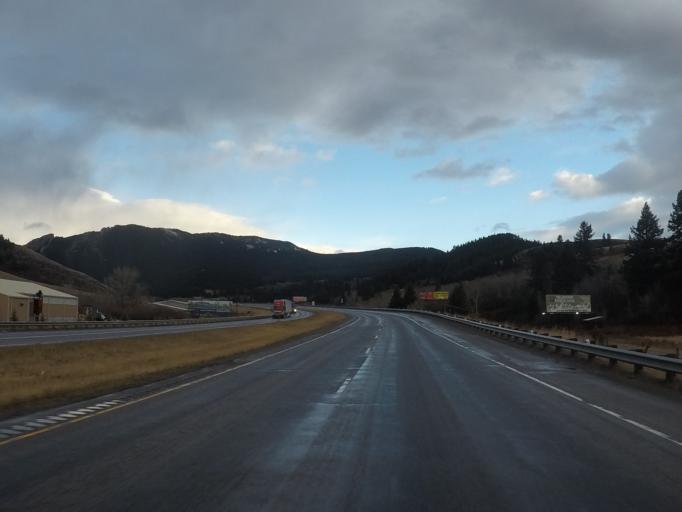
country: US
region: Montana
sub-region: Gallatin County
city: Bozeman
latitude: 45.6508
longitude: -110.9423
